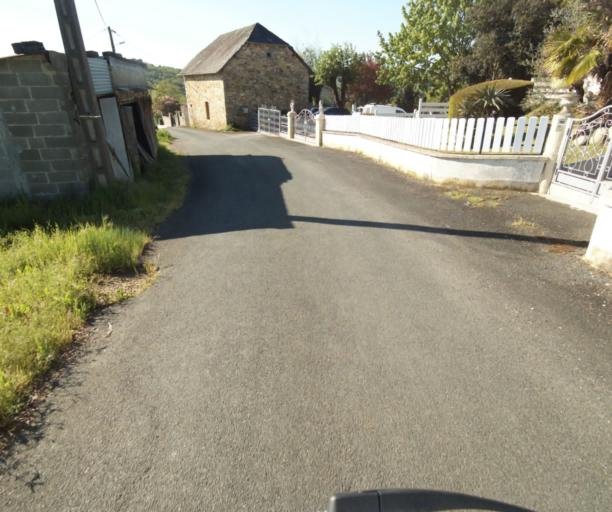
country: FR
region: Limousin
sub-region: Departement de la Correze
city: Tulle
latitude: 45.2606
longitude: 1.7738
